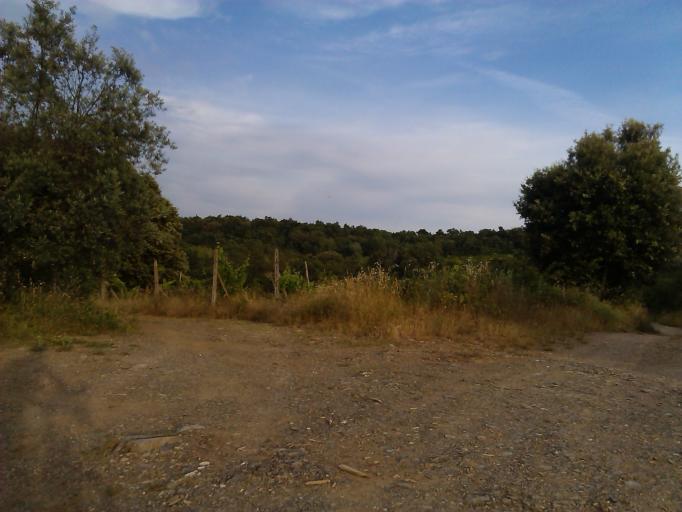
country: IT
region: Tuscany
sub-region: Province of Arezzo
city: Ponticino
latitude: 43.4644
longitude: 11.7297
